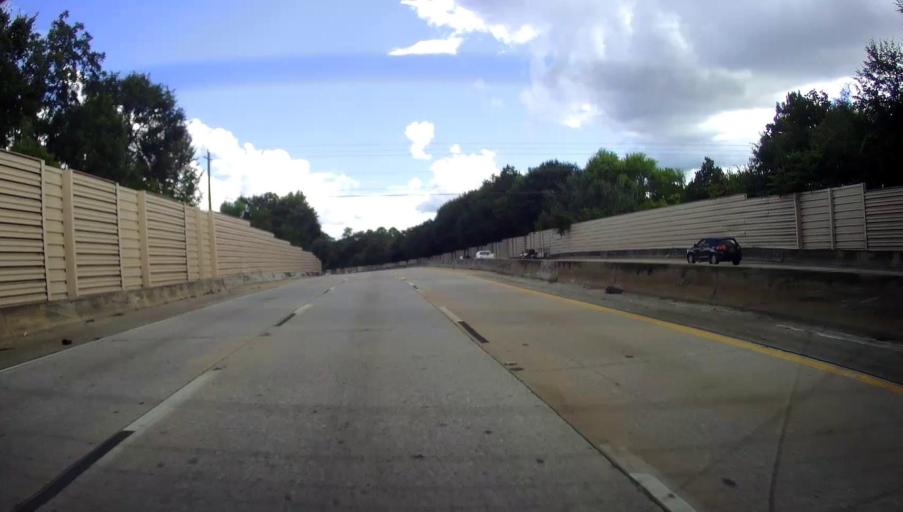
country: US
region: Georgia
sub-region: Muscogee County
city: Columbus
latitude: 32.4918
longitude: -84.9431
